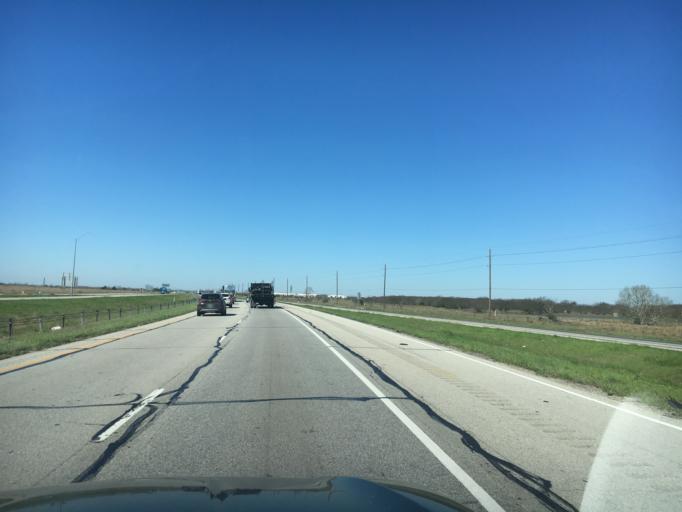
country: US
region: Texas
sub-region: Austin County
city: Sealy
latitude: 29.7640
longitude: -96.1901
